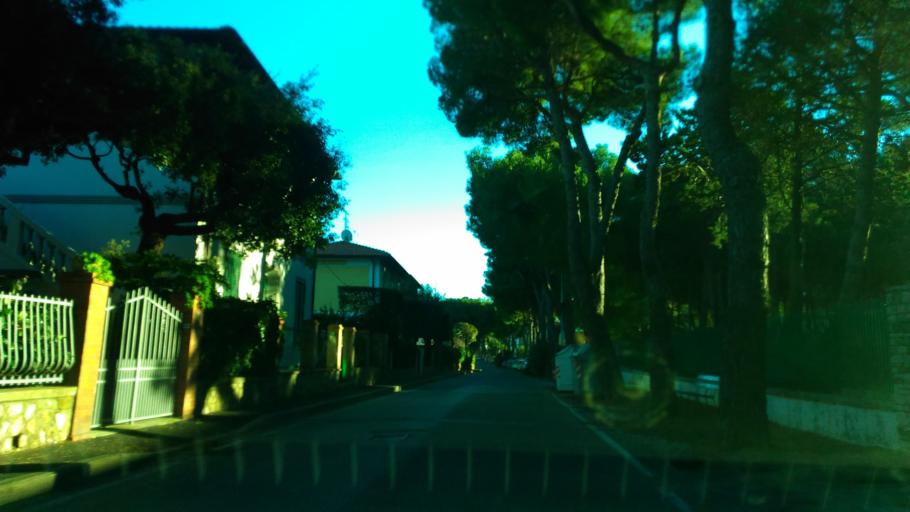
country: IT
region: Tuscany
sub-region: Provincia di Livorno
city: Quercianella
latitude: 43.4563
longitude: 10.3712
